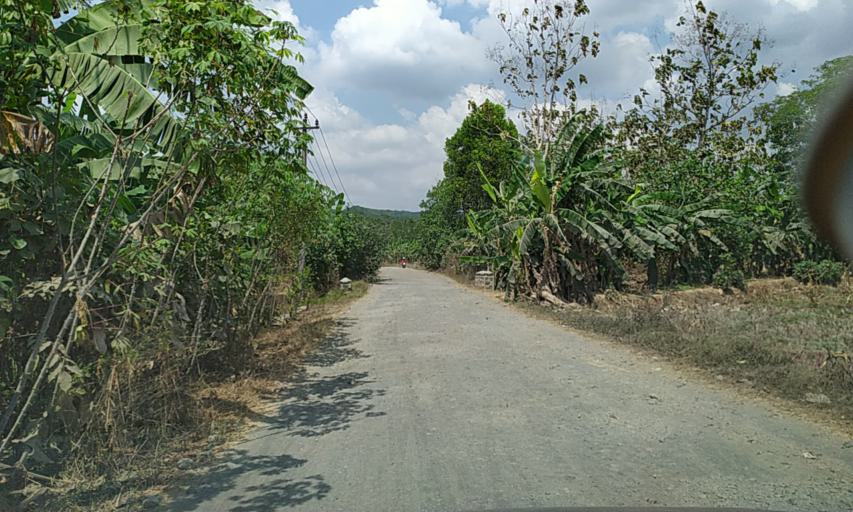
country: ID
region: Central Java
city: Cigintung
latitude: -7.3849
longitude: 108.8005
